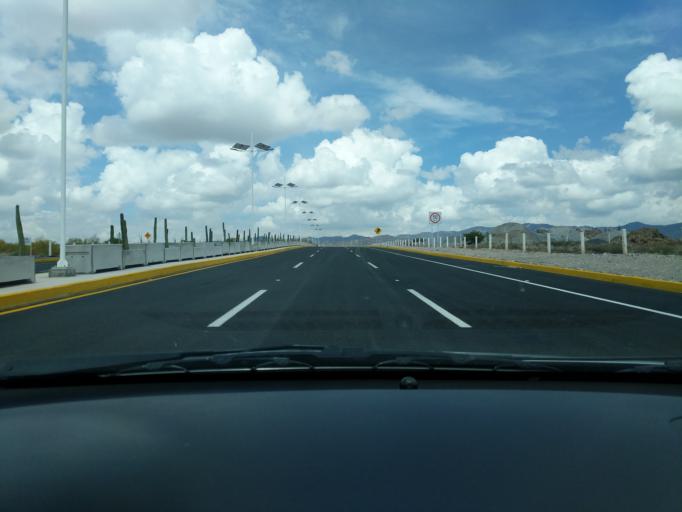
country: MX
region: San Luis Potosi
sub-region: Mexquitic de Carmona
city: Guadalupe Victoria
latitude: 22.1649
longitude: -101.0546
